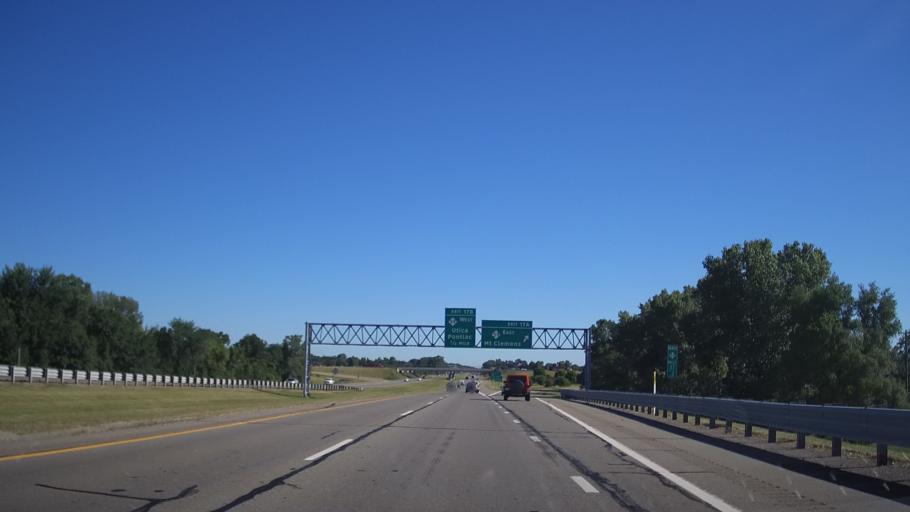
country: US
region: Michigan
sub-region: Macomb County
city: Utica
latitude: 42.6204
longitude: -83.0122
